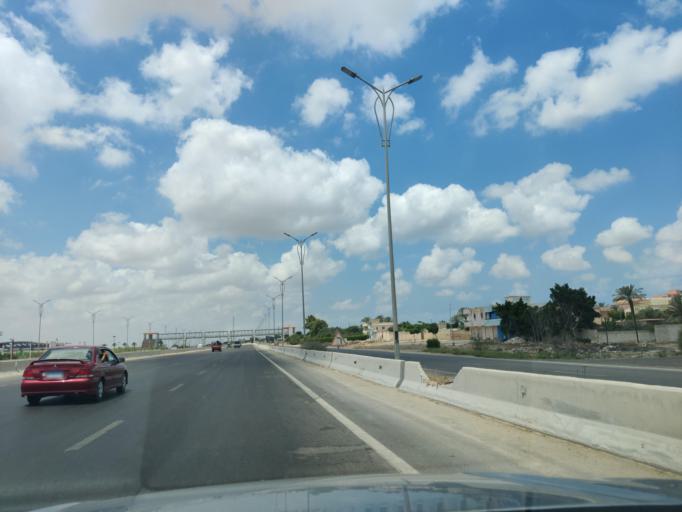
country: EG
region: Alexandria
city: Alexandria
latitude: 31.0079
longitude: 29.7381
